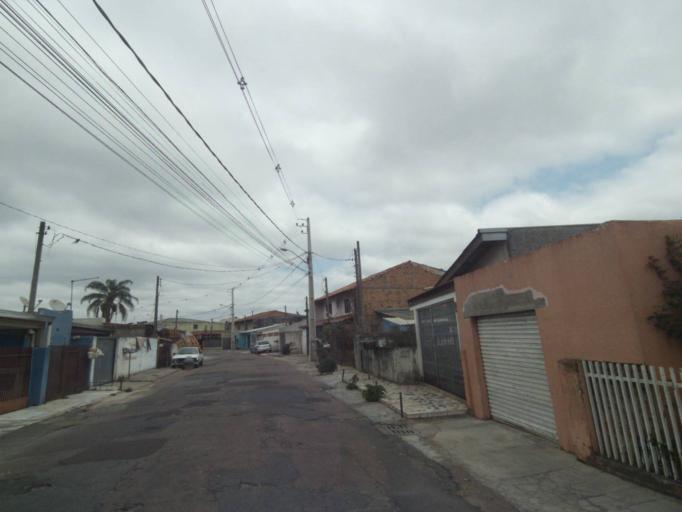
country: BR
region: Parana
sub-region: Sao Jose Dos Pinhais
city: Sao Jose dos Pinhais
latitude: -25.5359
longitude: -49.2645
